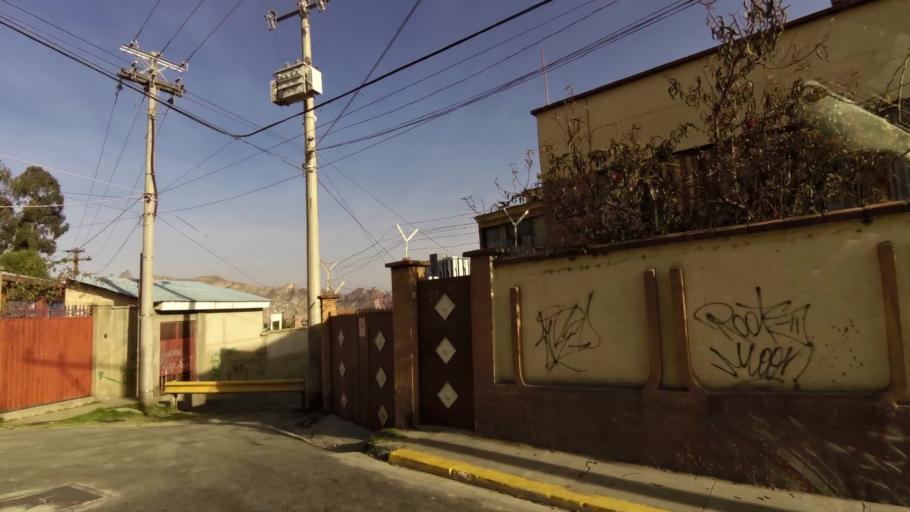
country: BO
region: La Paz
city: La Paz
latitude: -16.5267
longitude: -68.1018
